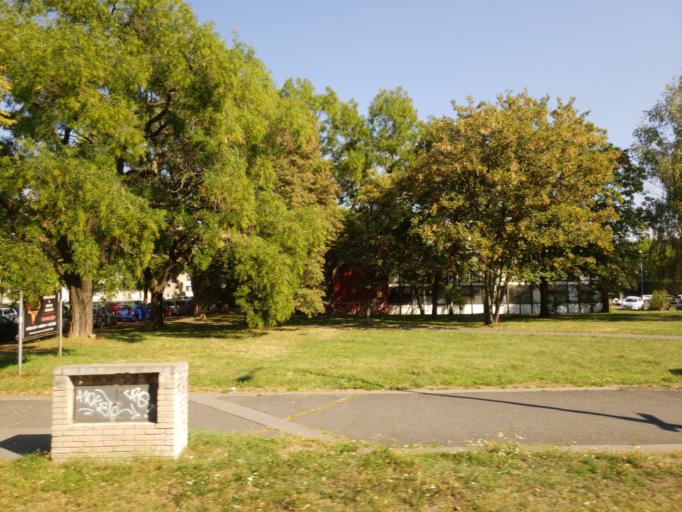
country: CZ
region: Praha
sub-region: Praha 1
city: Mala Strana
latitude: 50.0793
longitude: 14.3900
